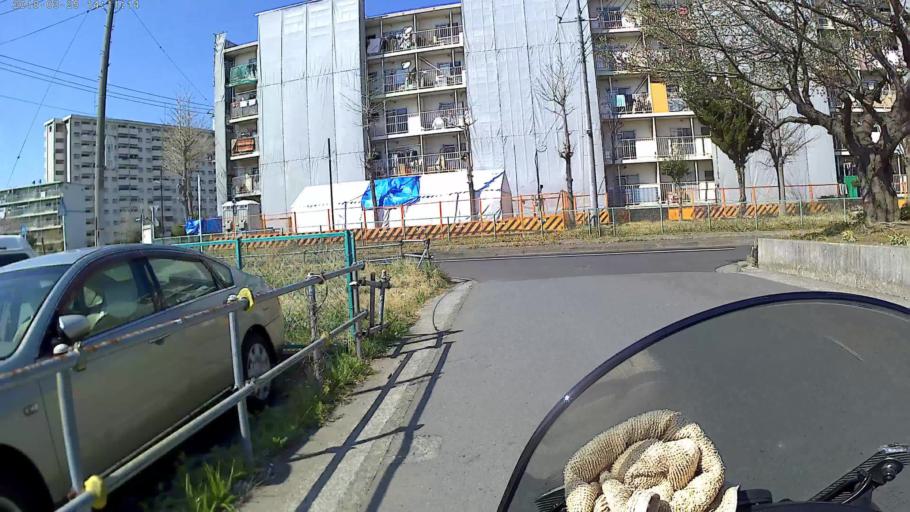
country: JP
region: Kanagawa
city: Minami-rinkan
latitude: 35.4271
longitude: 139.4734
